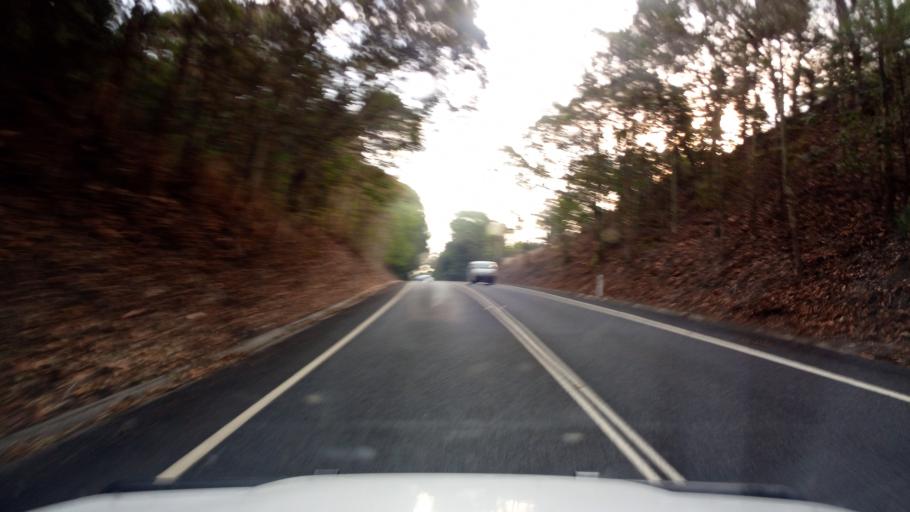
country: AU
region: Queensland
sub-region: Tablelands
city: Kuranda
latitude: -16.8420
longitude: 145.6108
